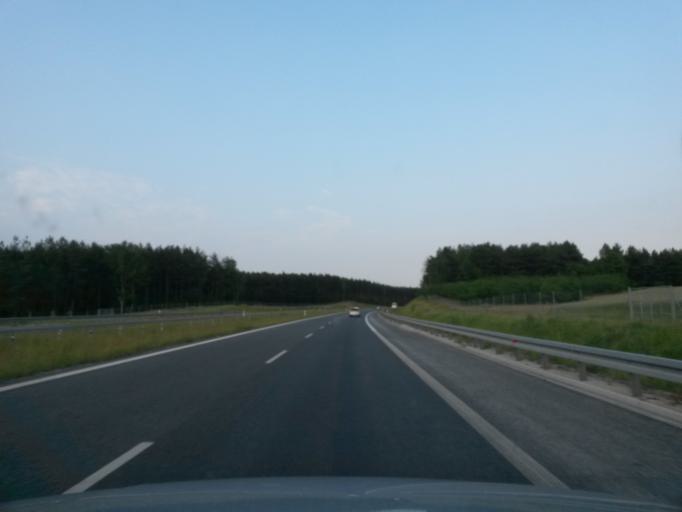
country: PL
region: Greater Poland Voivodeship
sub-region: Powiat kepinski
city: Perzow
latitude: 51.3033
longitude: 17.7810
